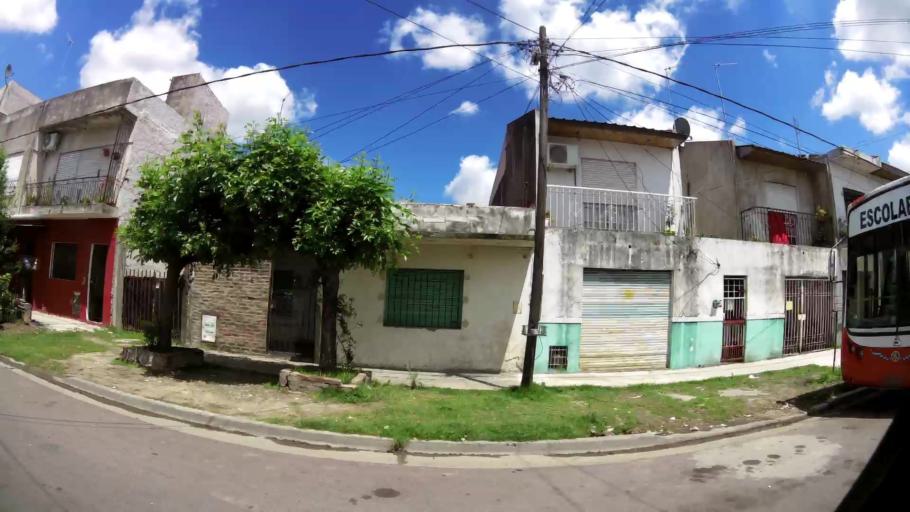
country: AR
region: Buenos Aires
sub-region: Partido de Lanus
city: Lanus
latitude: -34.6993
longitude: -58.4336
